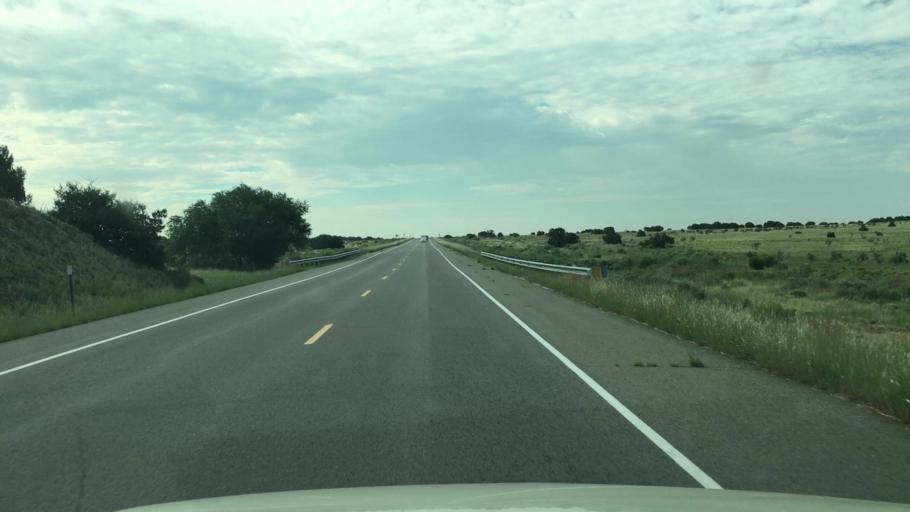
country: US
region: New Mexico
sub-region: Santa Fe County
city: Eldorado at Santa Fe
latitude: 35.4327
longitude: -105.8804
